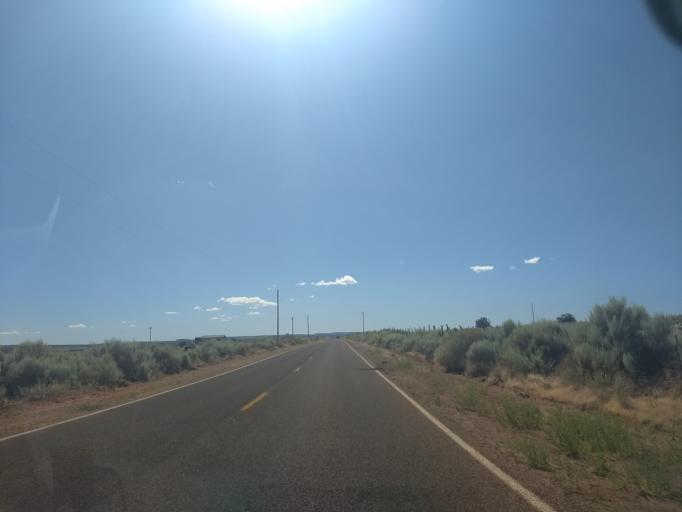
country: US
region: Arizona
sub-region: Mohave County
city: Colorado City
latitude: 36.9469
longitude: -112.9287
